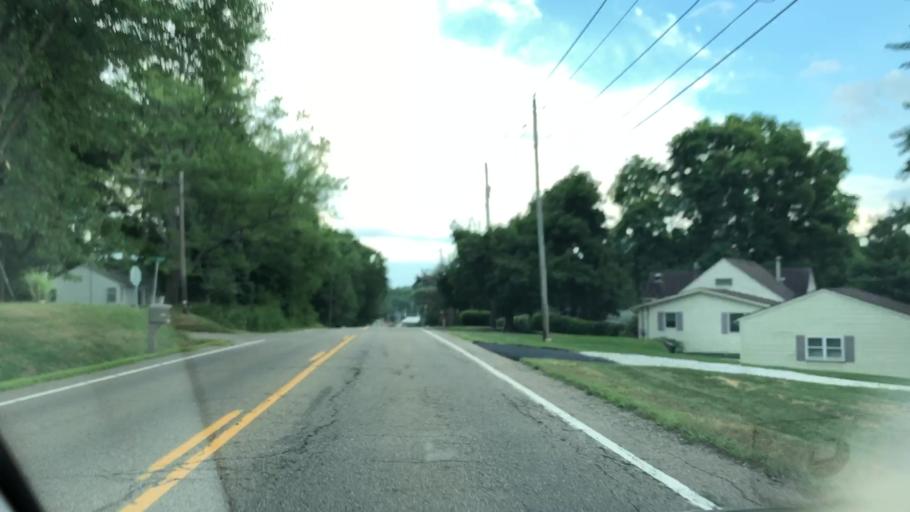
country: US
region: Ohio
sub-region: Summit County
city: Portage Lakes
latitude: 41.0009
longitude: -81.5604
